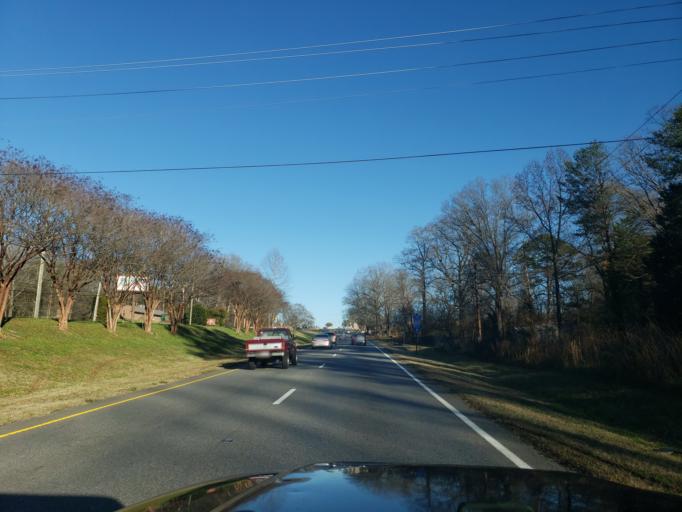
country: US
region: North Carolina
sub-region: Gaston County
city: Gastonia
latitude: 35.2578
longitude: -81.2334
